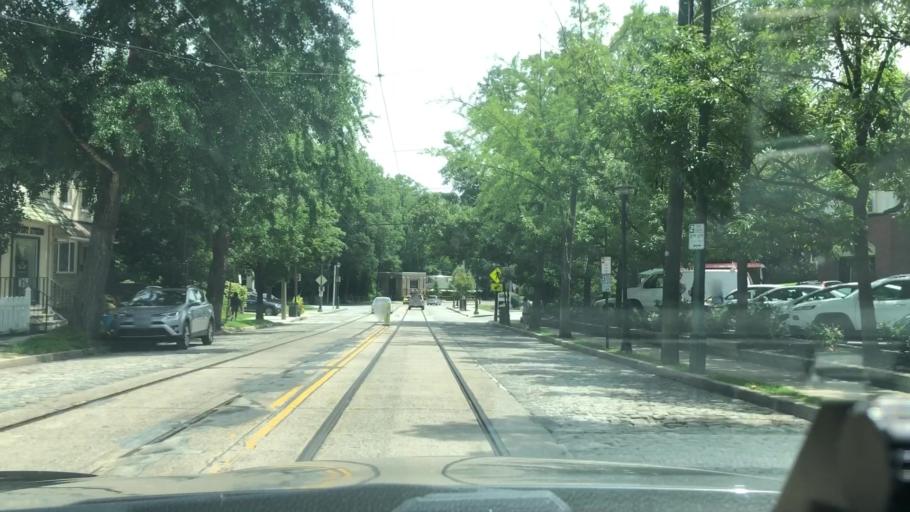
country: US
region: Pennsylvania
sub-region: Montgomery County
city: Wyndmoor
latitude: 40.0681
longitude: -75.1980
